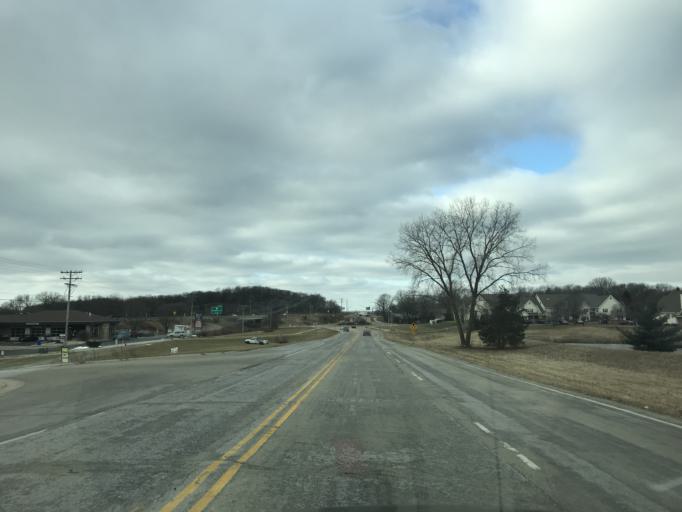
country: US
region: Wisconsin
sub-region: Dane County
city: Monona
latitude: 43.1065
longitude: -89.2968
